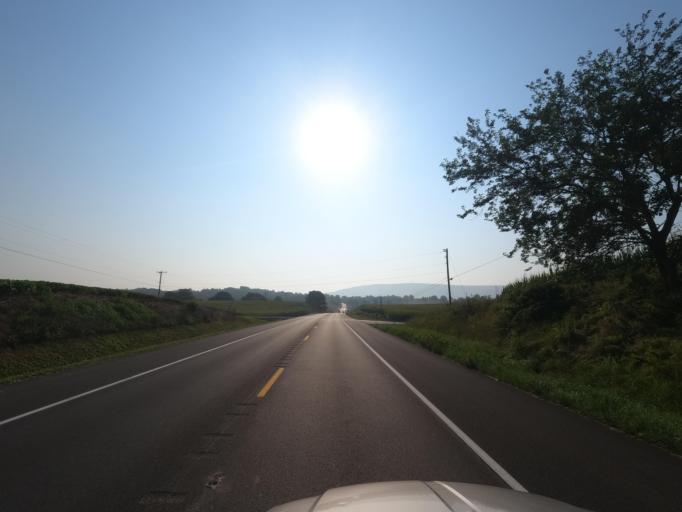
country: US
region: Pennsylvania
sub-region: Franklin County
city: Wayne Heights
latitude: 39.7079
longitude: -77.5797
